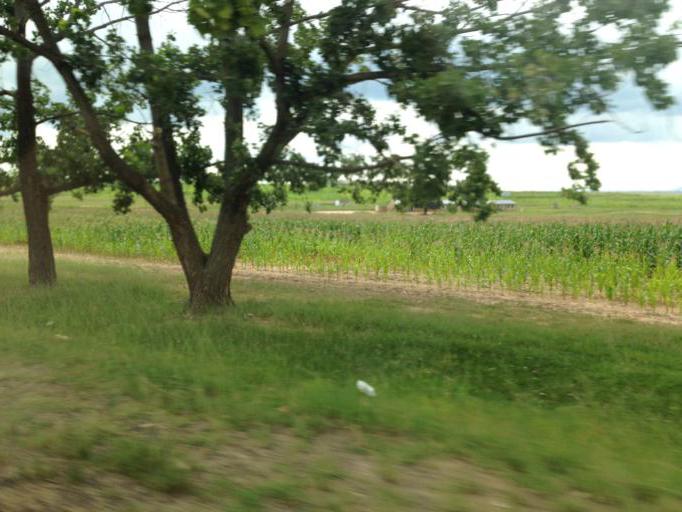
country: ZA
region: Orange Free State
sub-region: Thabo Mofutsanyana District Municipality
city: Ficksburg
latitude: -28.9630
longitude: 27.7865
